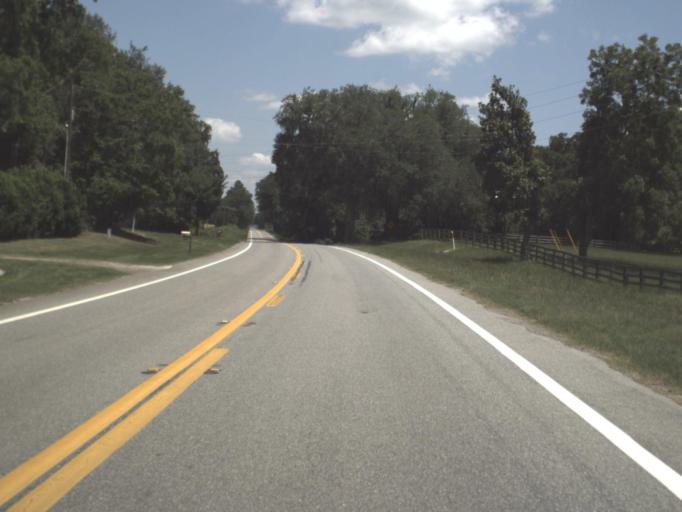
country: US
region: Florida
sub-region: Madison County
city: Madison
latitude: 30.5296
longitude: -83.6315
